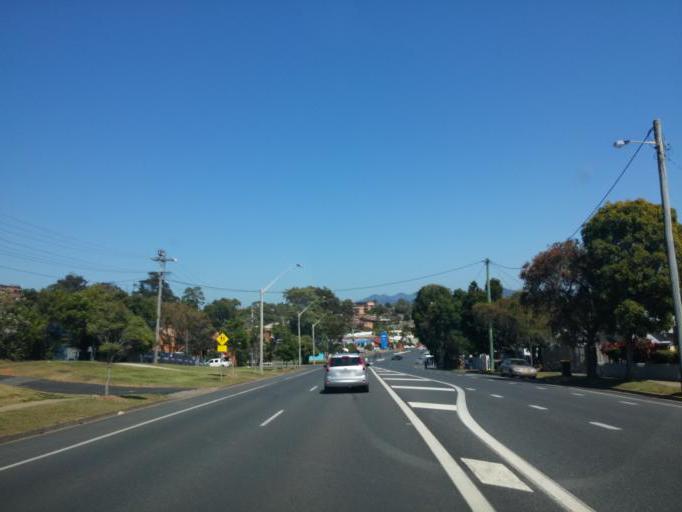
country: AU
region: New South Wales
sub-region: Coffs Harbour
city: Coffs Harbour
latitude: -30.3050
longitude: 153.1345
